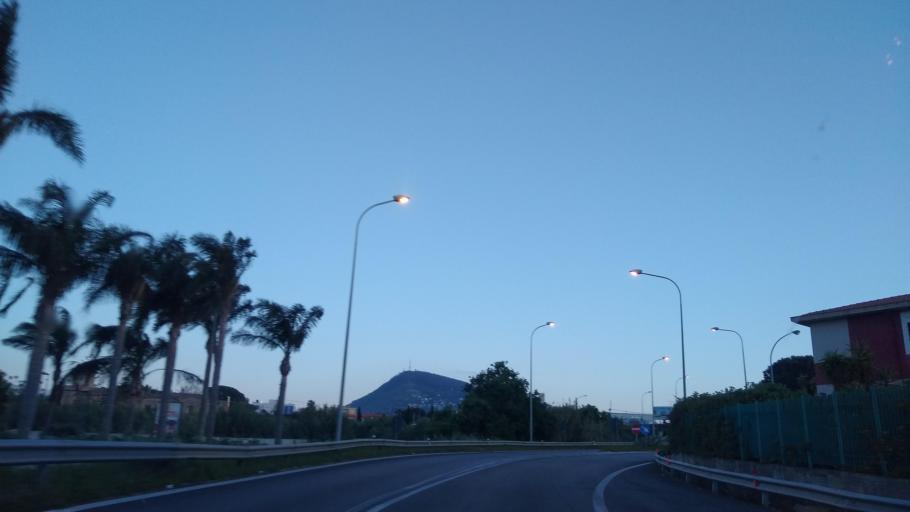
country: IT
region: Sicily
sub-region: Trapani
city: Alcamo
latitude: 38.0007
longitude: 12.9576
